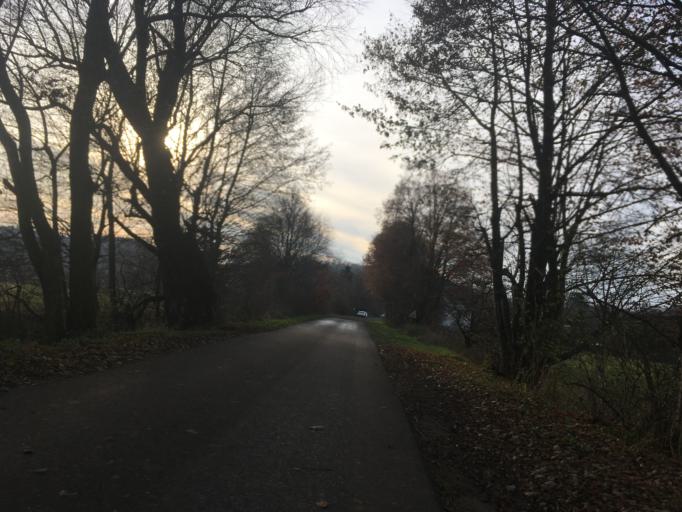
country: DE
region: Brandenburg
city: Falkenberg
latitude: 52.8090
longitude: 13.9637
